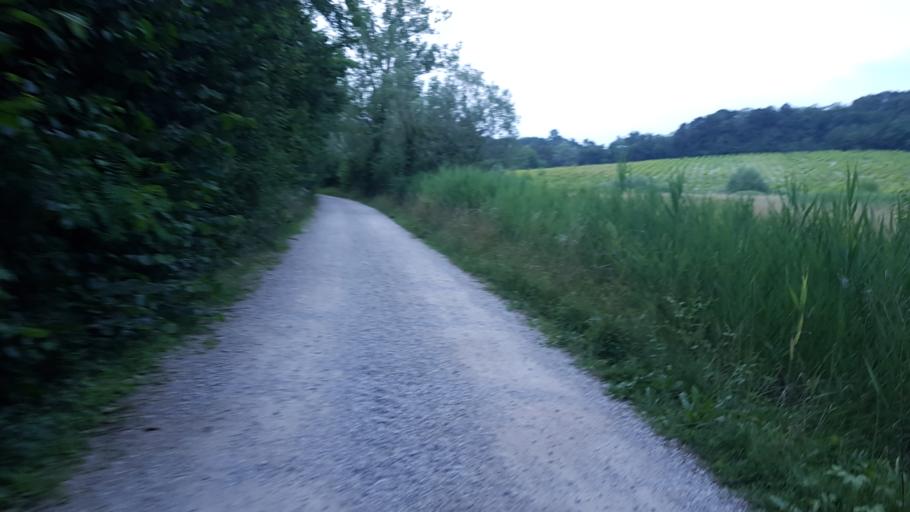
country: IT
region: Friuli Venezia Giulia
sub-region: Provincia di Gorizia
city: San Lorenzo Isontino
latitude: 45.9389
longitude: 13.5276
